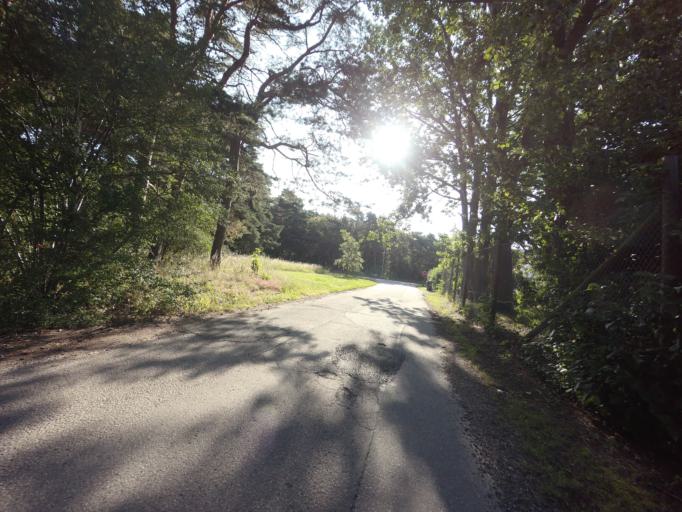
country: SE
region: Skane
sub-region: Kavlinge Kommun
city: Hofterup
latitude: 55.8317
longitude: 12.9618
